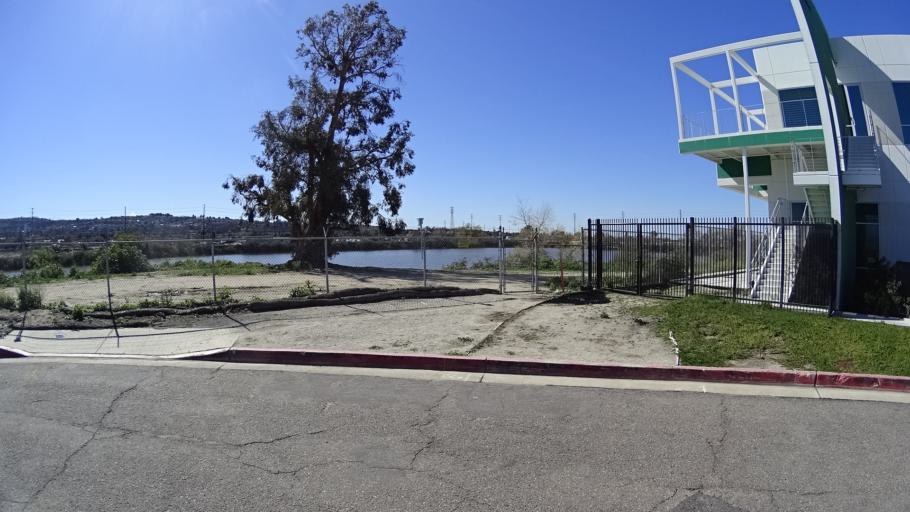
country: US
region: California
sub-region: Orange County
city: Yorba Linda
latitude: 33.8579
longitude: -117.8235
